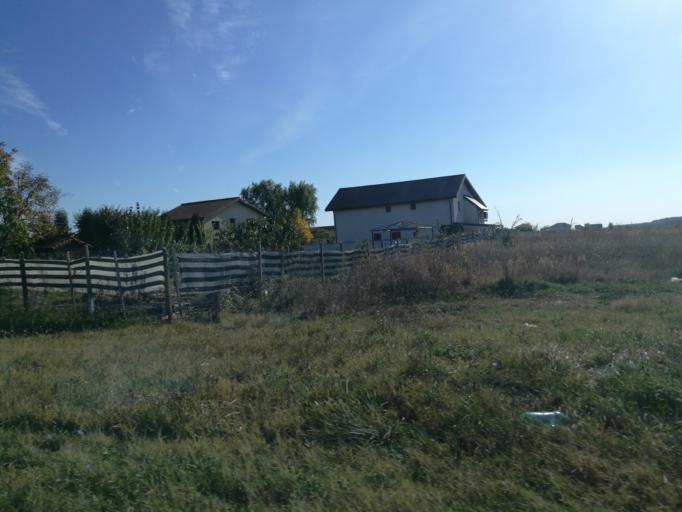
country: RO
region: Ilfov
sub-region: Comuna Dragomiresti-Vale
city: Dragomiresti-Deal
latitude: 44.4639
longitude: 25.9345
